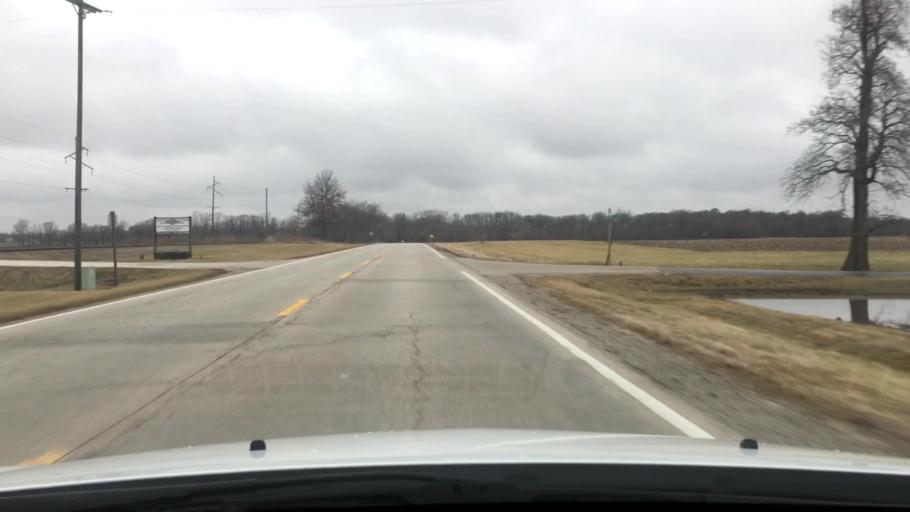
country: US
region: Illinois
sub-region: Iroquois County
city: Sheldon
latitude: 40.8092
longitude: -87.5754
